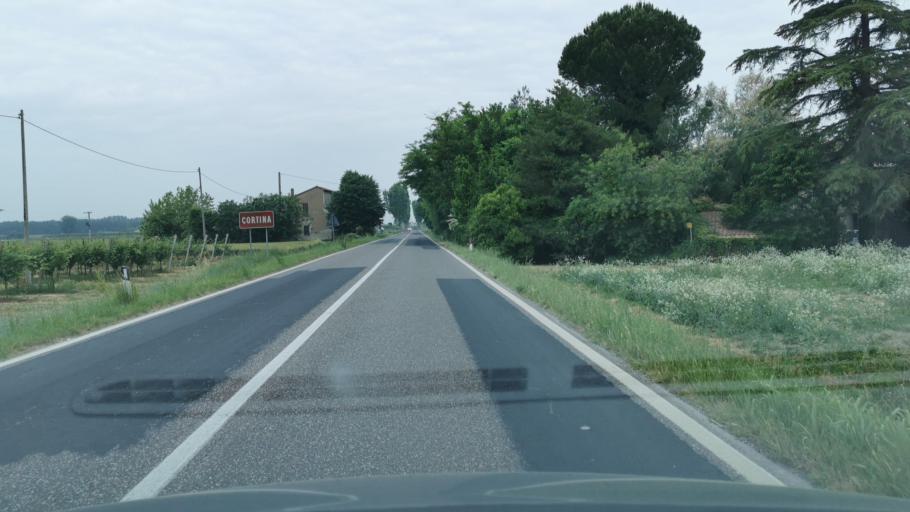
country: IT
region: Emilia-Romagna
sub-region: Provincia di Ravenna
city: Russi
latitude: 44.3977
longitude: 12.0330
